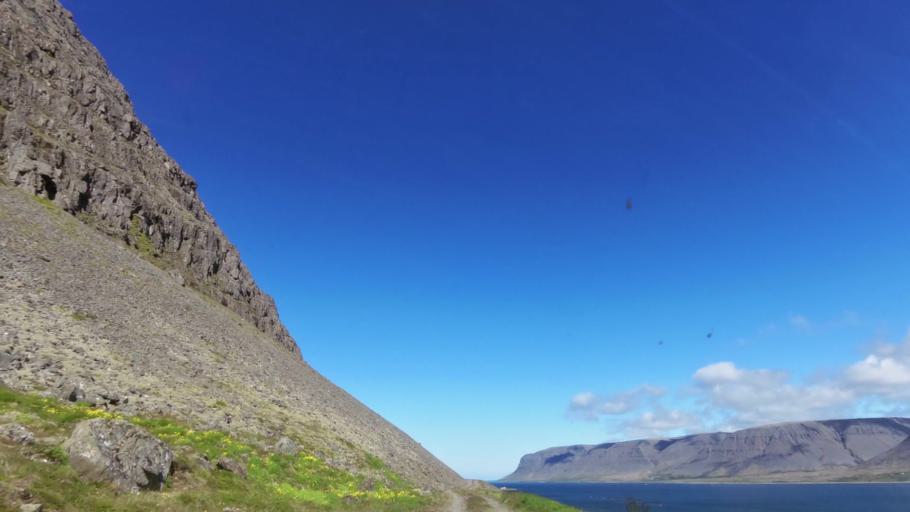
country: IS
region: West
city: Olafsvik
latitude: 65.6266
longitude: -23.9009
